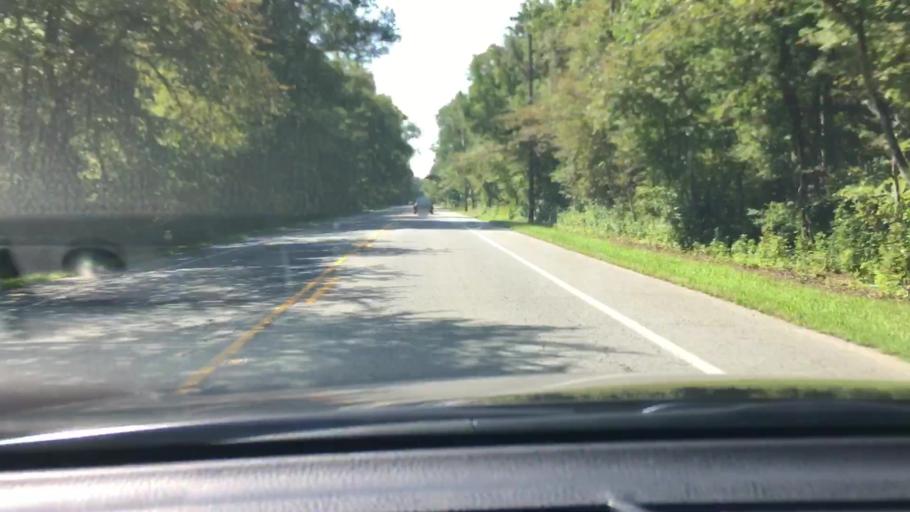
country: US
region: New Jersey
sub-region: Cape May County
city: Woodbine
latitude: 39.2581
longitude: -74.8058
